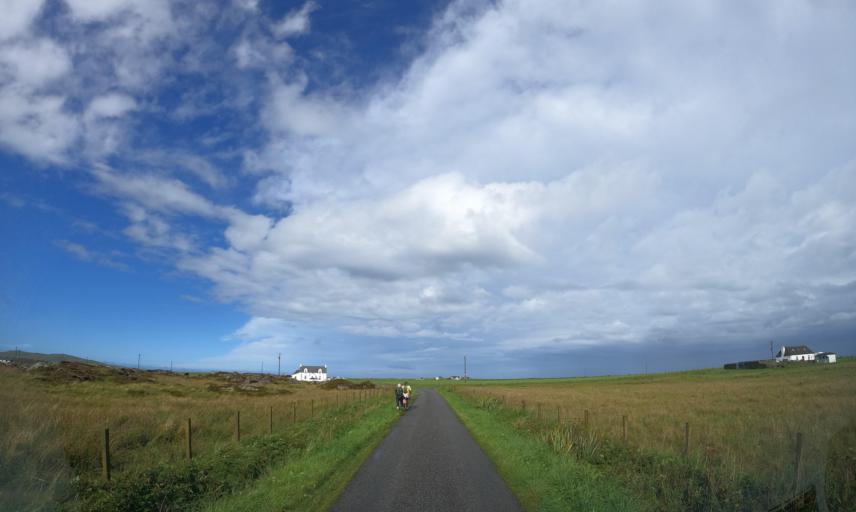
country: GB
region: Scotland
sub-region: Eilean Siar
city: Barra
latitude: 56.5204
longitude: -6.8941
